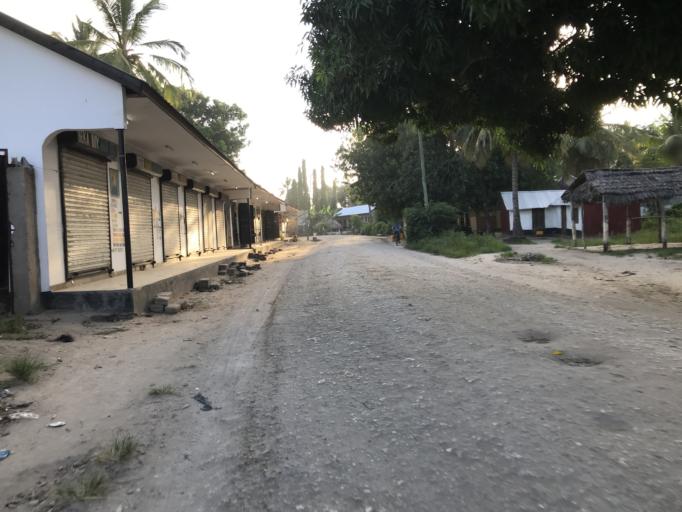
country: TZ
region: Dar es Salaam
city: Dar es Salaam
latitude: -6.8636
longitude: 39.3559
